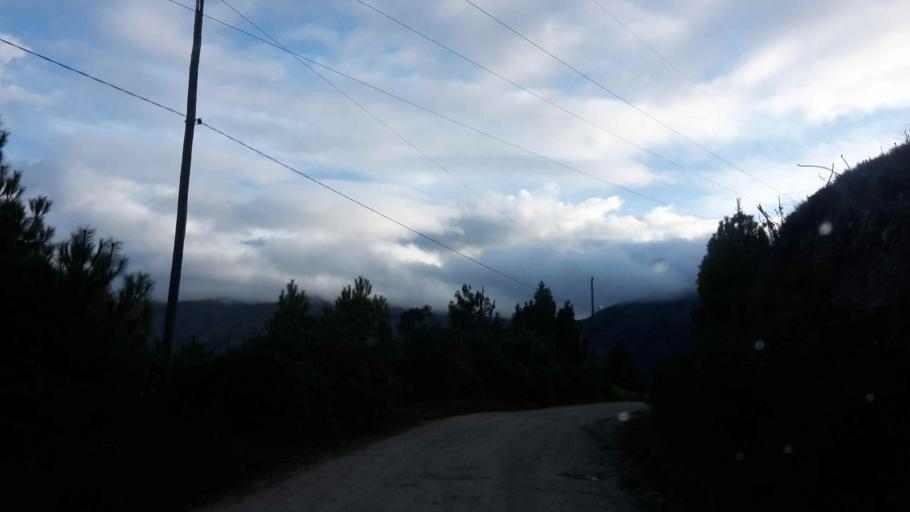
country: BO
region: Cochabamba
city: Colomi
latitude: -17.2768
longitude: -65.9098
